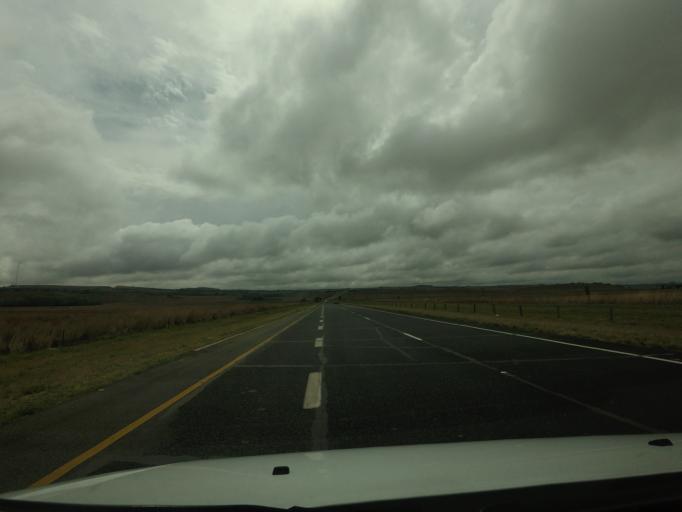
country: ZA
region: Mpumalanga
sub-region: Nkangala District Municipality
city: Middelburg
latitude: -25.8544
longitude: 29.3831
